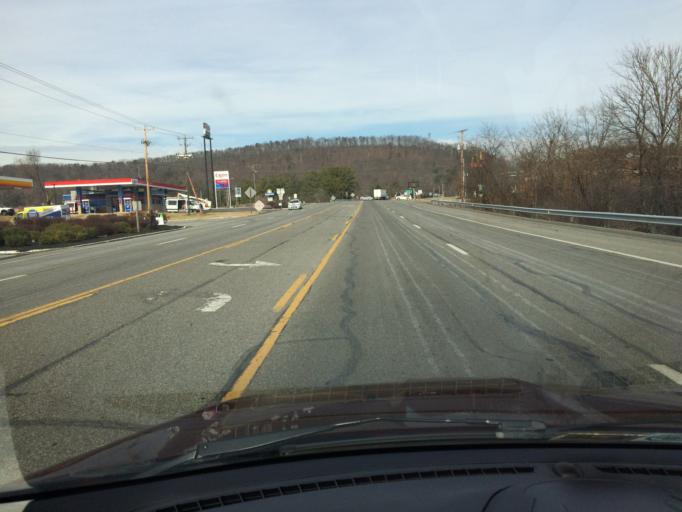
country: US
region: Virginia
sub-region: Roanoke County
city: Hollins
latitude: 37.3580
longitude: -79.9567
